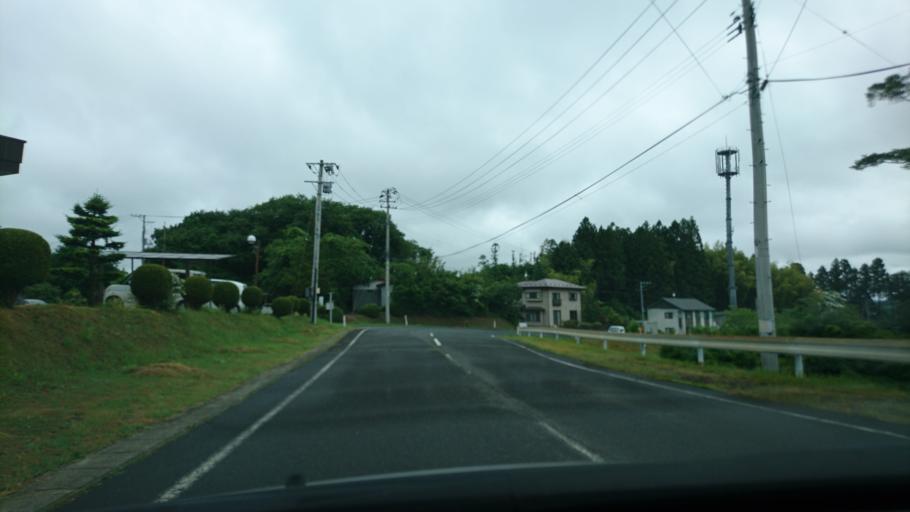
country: JP
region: Iwate
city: Ichinoseki
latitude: 38.8819
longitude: 141.1402
